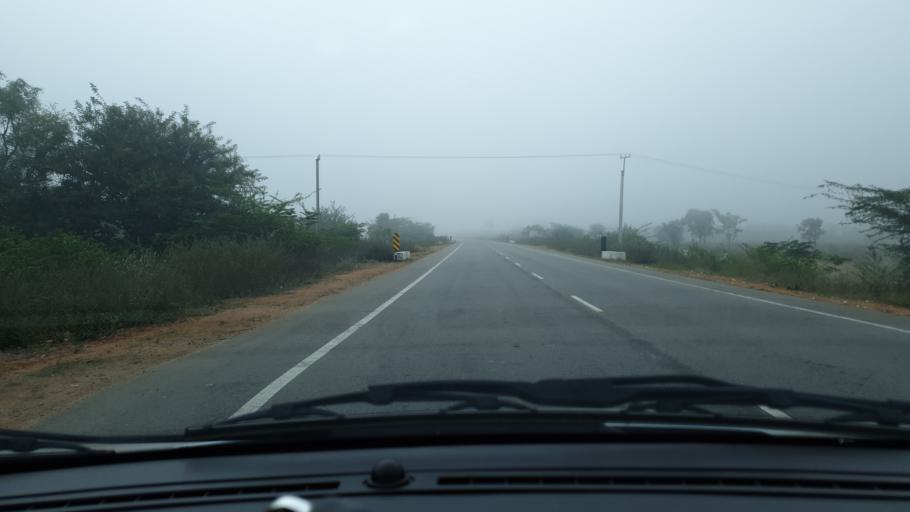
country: IN
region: Telangana
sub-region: Nalgonda
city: Devarkonda
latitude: 16.6052
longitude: 78.6788
